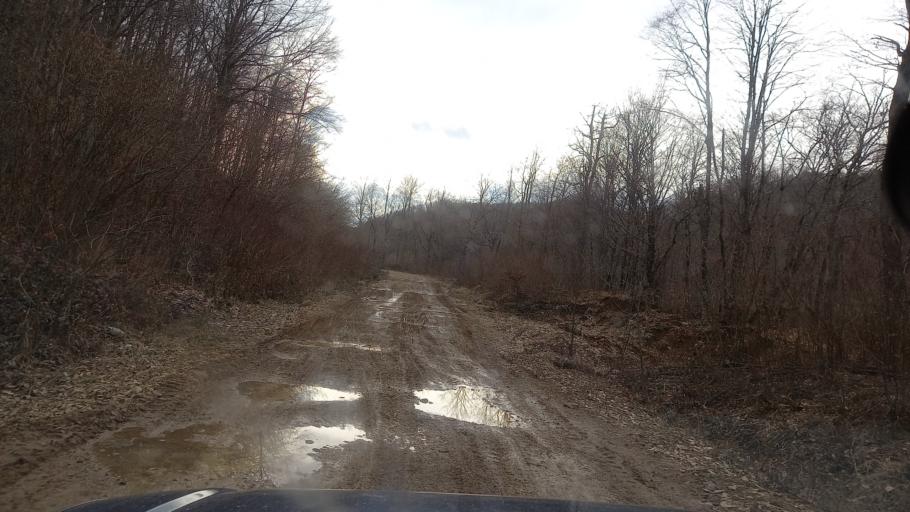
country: RU
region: Adygeya
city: Kamennomostskiy
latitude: 44.1704
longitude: 40.2983
